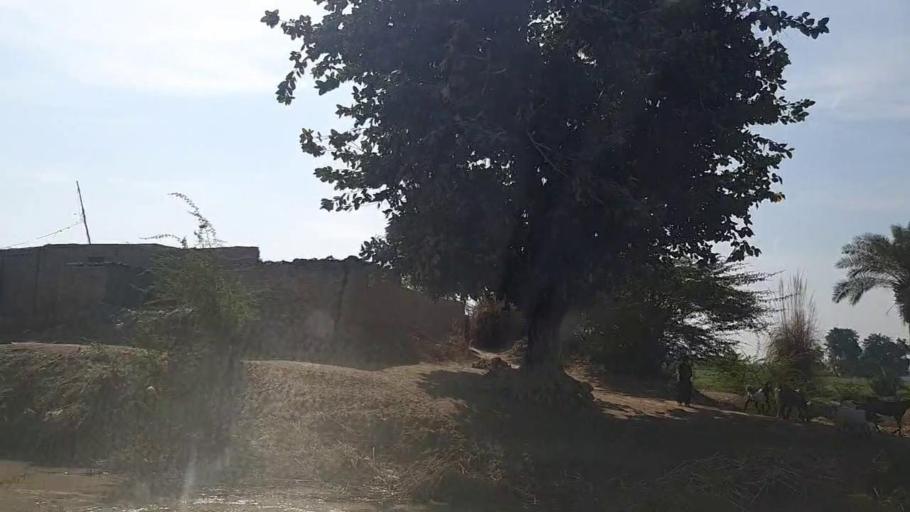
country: PK
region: Sindh
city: Mirpur Khas
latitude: 25.4690
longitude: 68.9744
